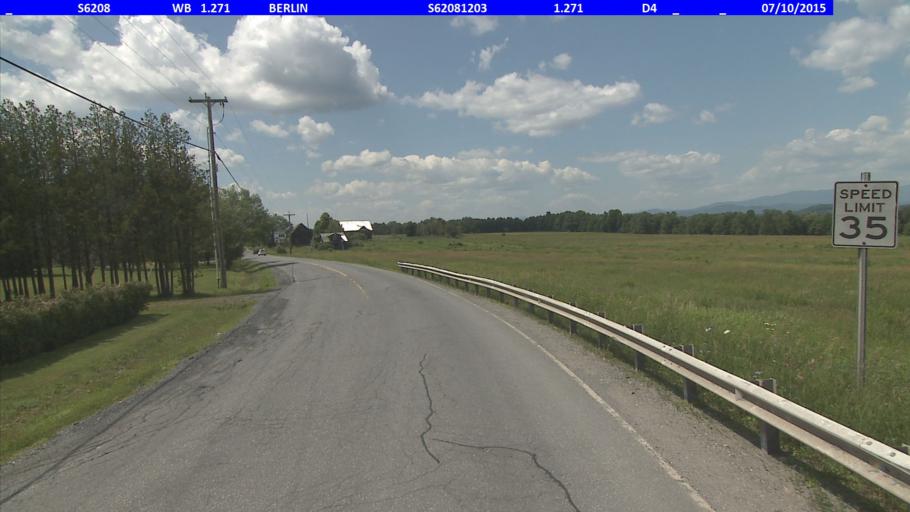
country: US
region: Vermont
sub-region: Washington County
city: Montpelier
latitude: 44.1971
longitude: -72.5663
